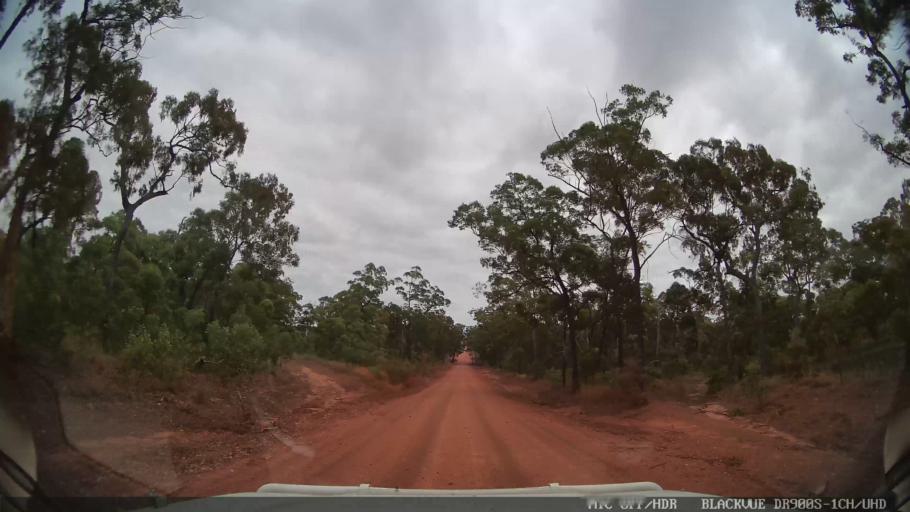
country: AU
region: Queensland
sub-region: Cook
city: Cooktown
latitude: -15.2647
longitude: 144.9523
